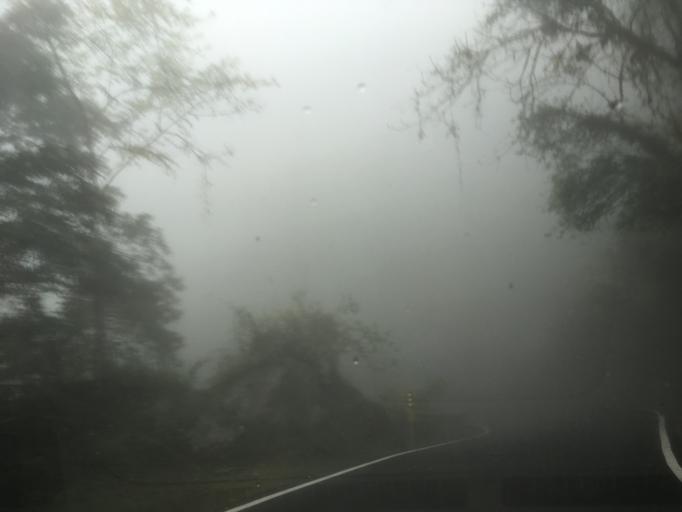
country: TW
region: Taiwan
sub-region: Hualien
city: Hualian
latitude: 24.1967
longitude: 121.4294
